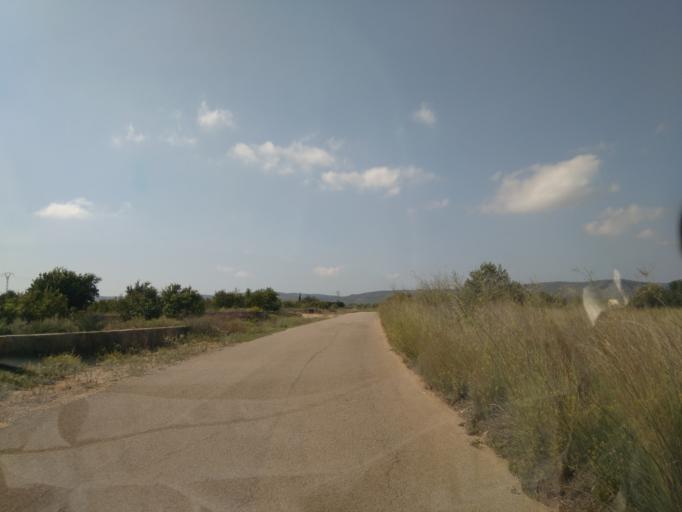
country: ES
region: Valencia
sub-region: Provincia de Valencia
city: Tous
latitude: 39.1676
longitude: -0.5710
